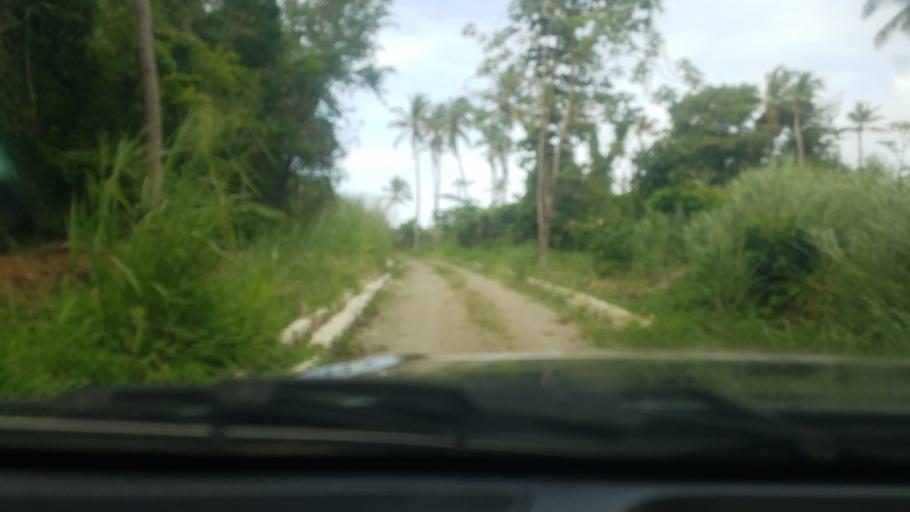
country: LC
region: Micoud Quarter
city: Micoud
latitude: 13.7985
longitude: -60.9235
